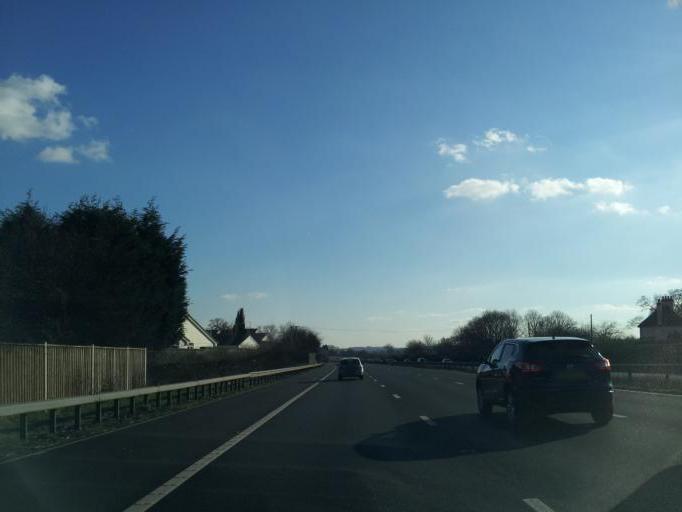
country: GB
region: England
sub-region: Devon
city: Cullompton
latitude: 50.8918
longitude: -3.3765
